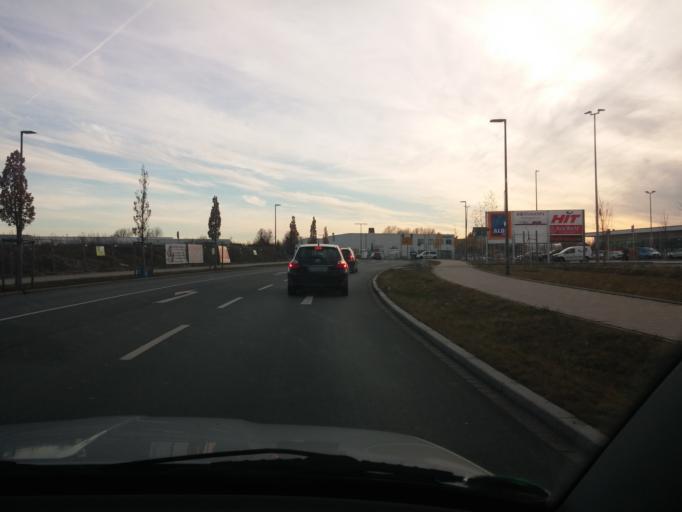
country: DE
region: Bavaria
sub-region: Upper Bavaria
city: Poing
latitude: 48.1466
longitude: 11.7892
